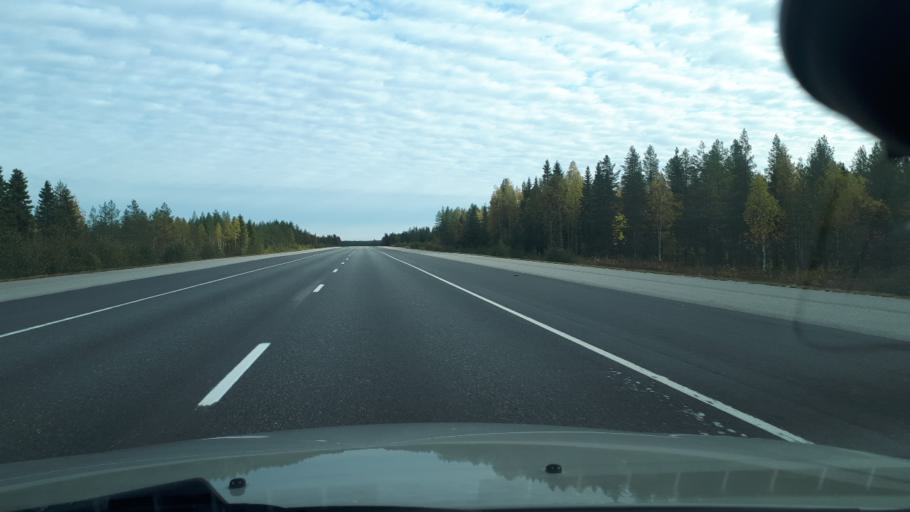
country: FI
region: Northern Ostrobothnia
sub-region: Oulu
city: Yli-Ii
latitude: 65.8945
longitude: 25.6938
